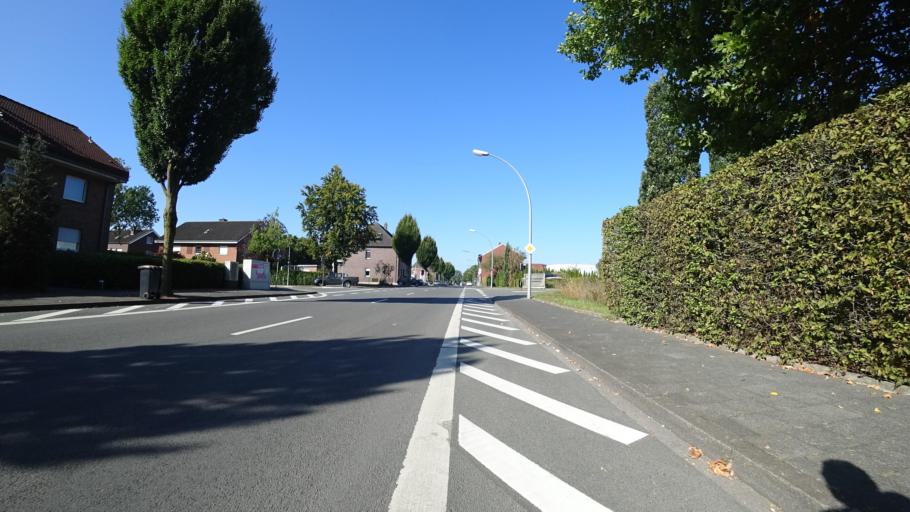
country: DE
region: North Rhine-Westphalia
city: Oelde
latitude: 51.8246
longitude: 8.1321
